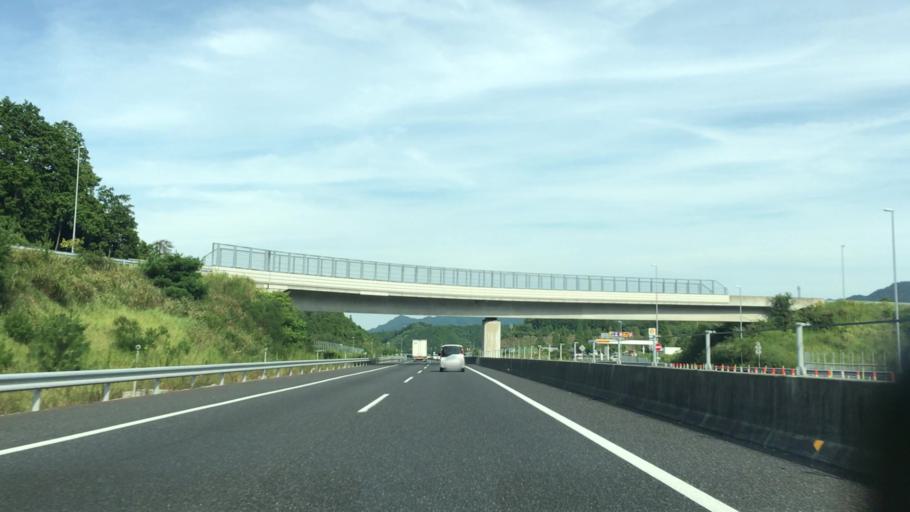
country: JP
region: Shiga Prefecture
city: Hino
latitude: 34.9165
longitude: 136.2893
